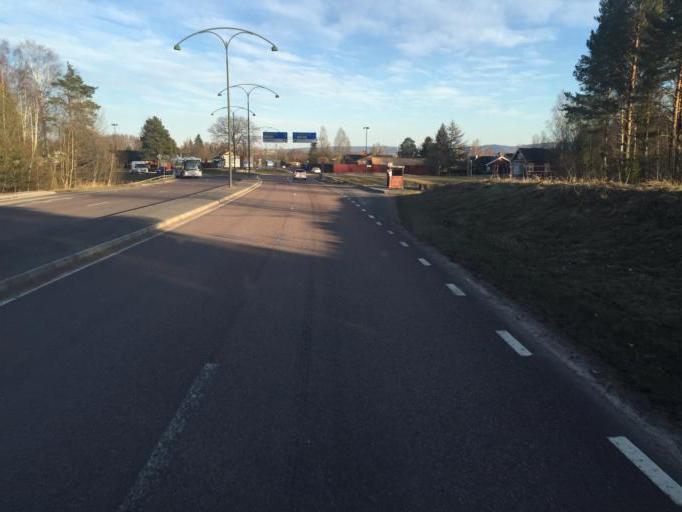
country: SE
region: Dalarna
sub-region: Borlange Kommun
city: Borlaenge
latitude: 60.5016
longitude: 15.3918
